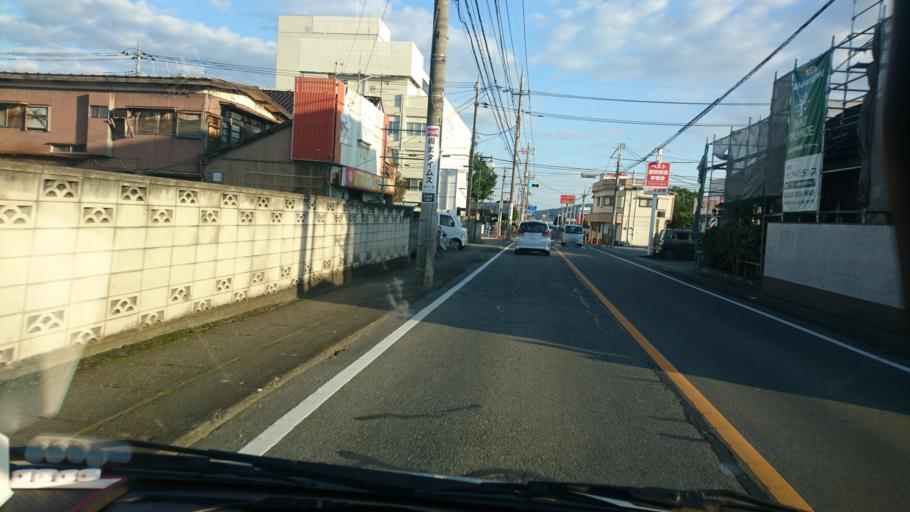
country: JP
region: Gunma
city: Kiryu
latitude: 36.3952
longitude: 139.3257
